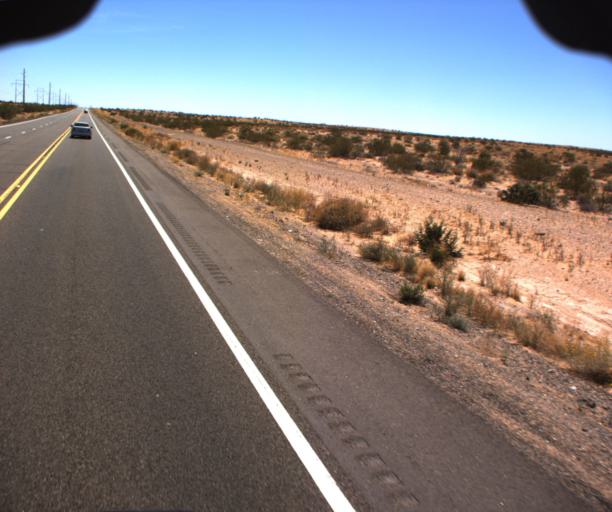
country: US
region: Arizona
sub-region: La Paz County
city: Parker
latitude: 33.9656
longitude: -114.2169
